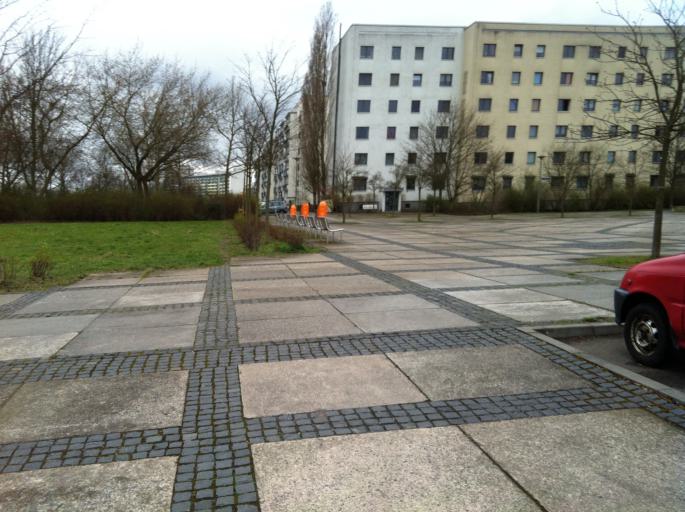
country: DE
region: Berlin
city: Kaulsdorf
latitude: 52.5275
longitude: 13.5888
